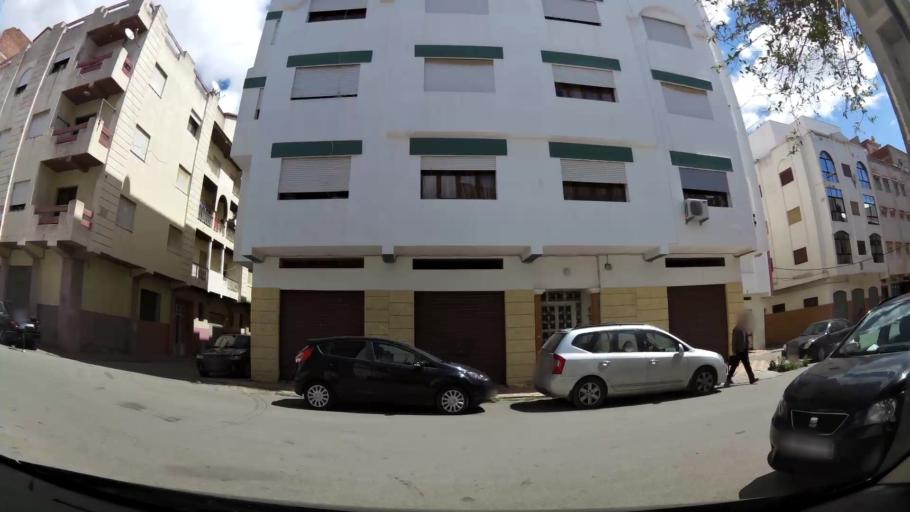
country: MA
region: Tanger-Tetouan
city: Tetouan
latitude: 35.5780
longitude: -5.3430
